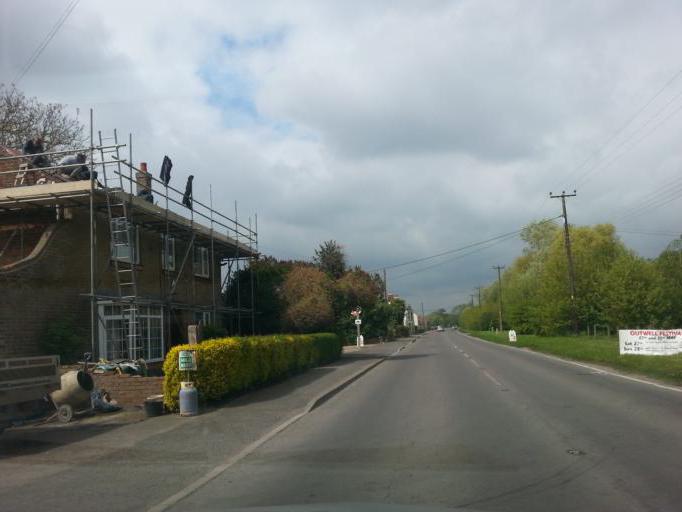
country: GB
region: England
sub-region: Norfolk
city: Outwell
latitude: 52.6123
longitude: 0.2328
